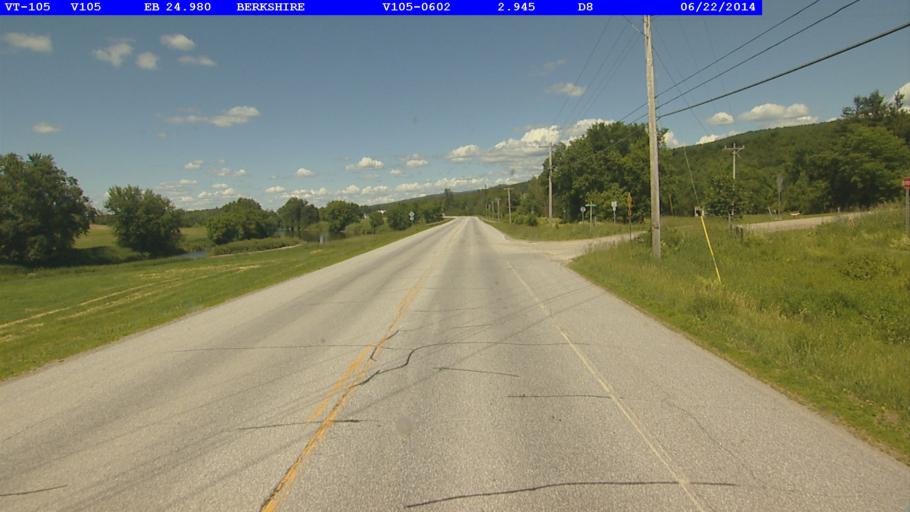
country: US
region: Vermont
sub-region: Franklin County
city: Richford
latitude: 44.9613
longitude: -72.6940
